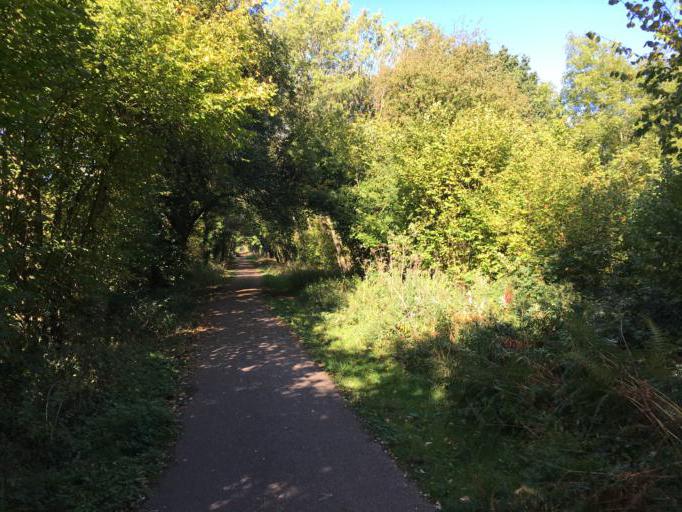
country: GB
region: England
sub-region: Warwickshire
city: Kenilworth
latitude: 52.3646
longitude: -1.5772
